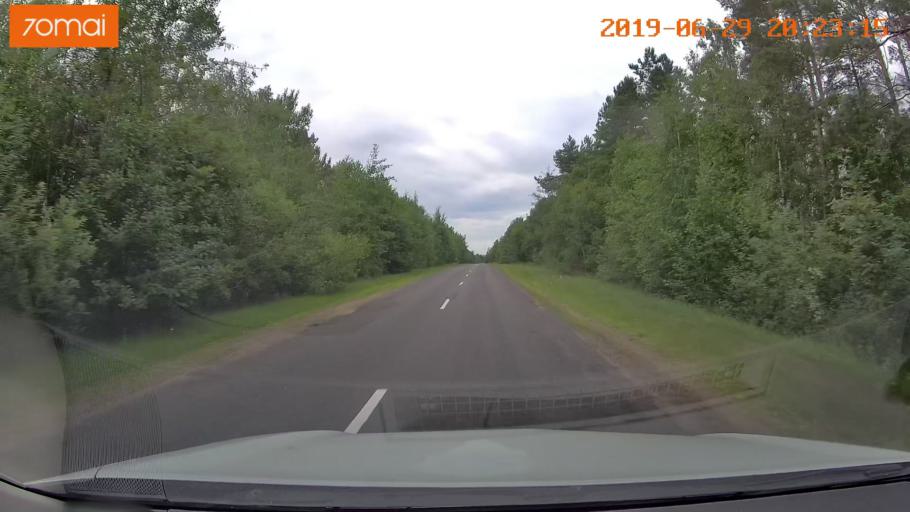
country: BY
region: Brest
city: Asnyezhytsy
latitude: 52.4420
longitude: 26.2594
